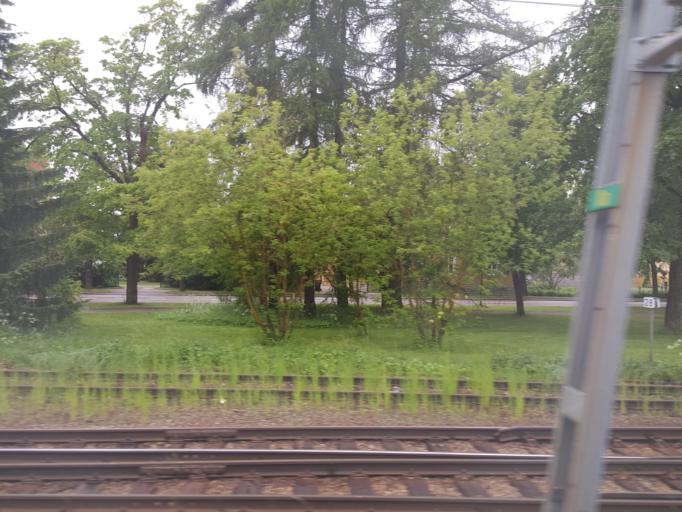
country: SE
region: Vaestmanland
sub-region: Sala Kommun
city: Sala
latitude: 59.9243
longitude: 16.6094
